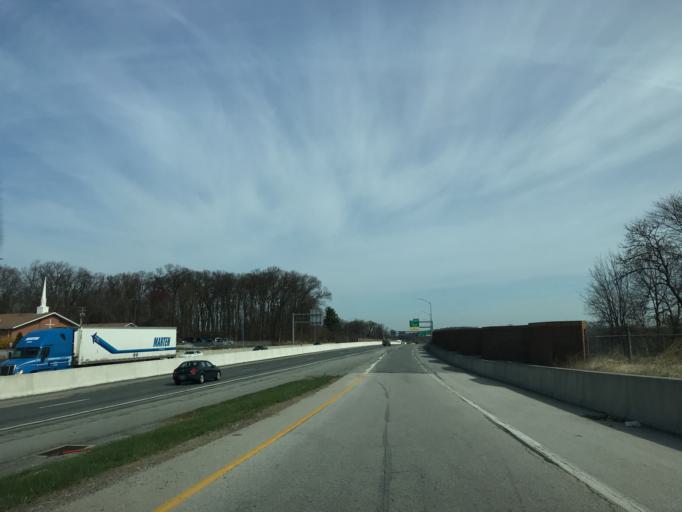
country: US
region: Pennsylvania
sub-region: York County
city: Spry
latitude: 39.9114
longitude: -76.7032
